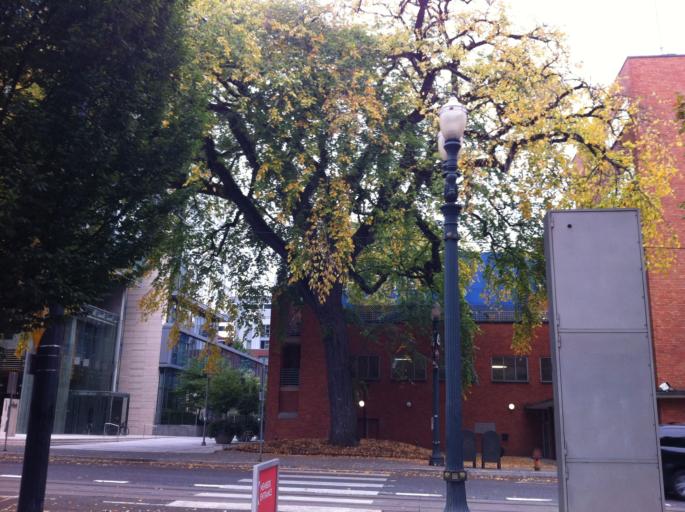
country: US
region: Oregon
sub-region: Multnomah County
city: Portland
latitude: 45.5167
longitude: -122.6838
